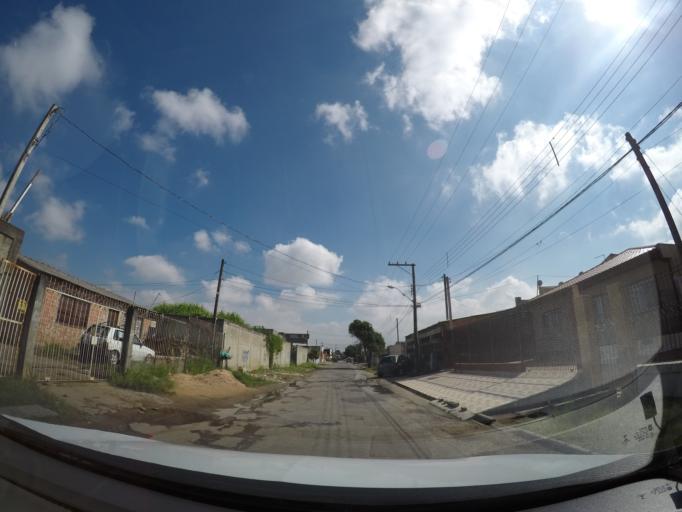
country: BR
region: Parana
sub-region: Sao Jose Dos Pinhais
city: Sao Jose dos Pinhais
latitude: -25.5000
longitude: -49.2206
